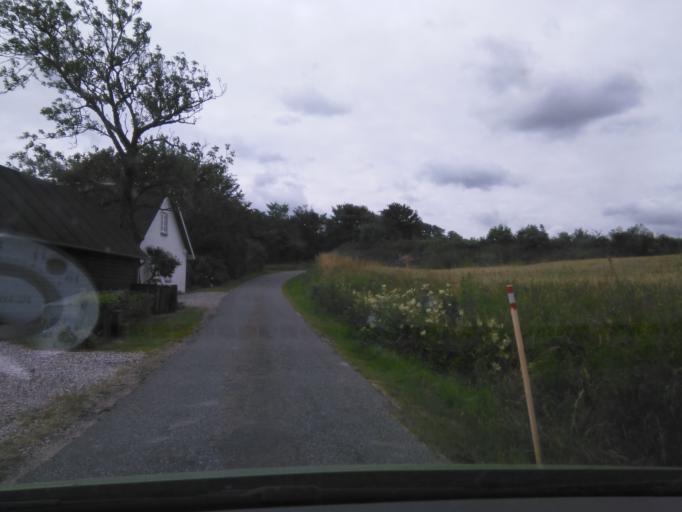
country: DK
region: Central Jutland
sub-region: Arhus Kommune
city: Solbjerg
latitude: 55.9914
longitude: 10.0452
